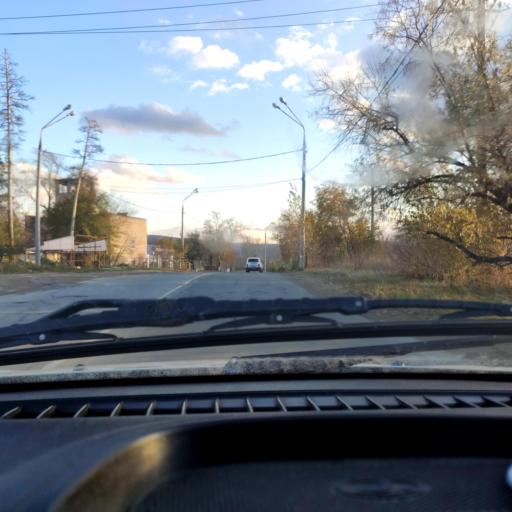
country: RU
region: Samara
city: Zhigulevsk
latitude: 53.4674
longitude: 49.5485
